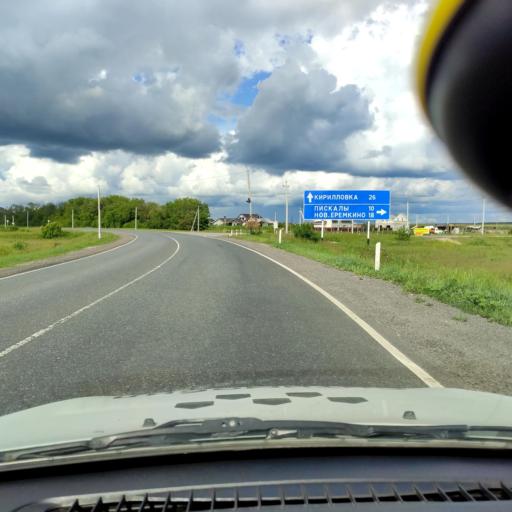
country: RU
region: Samara
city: Povolzhskiy
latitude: 53.6571
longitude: 49.7051
